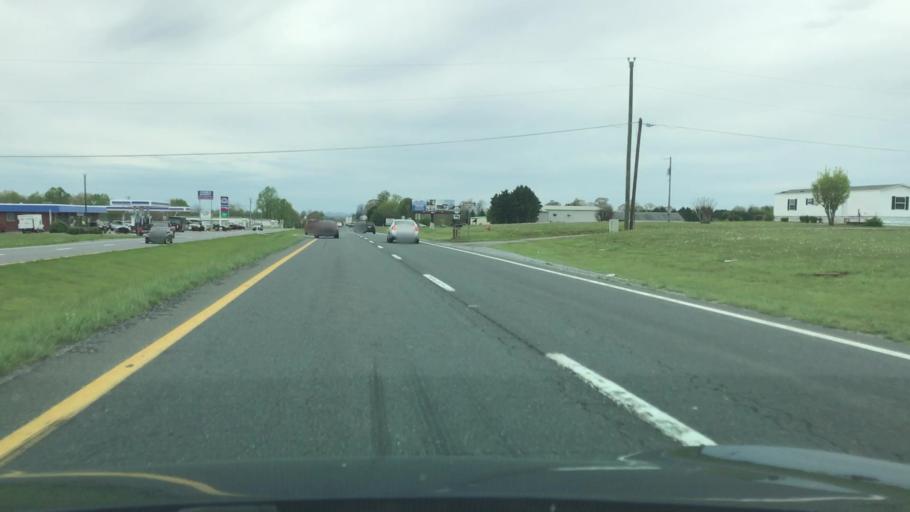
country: US
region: Virginia
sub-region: Bedford County
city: Forest
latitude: 37.3008
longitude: -79.3510
